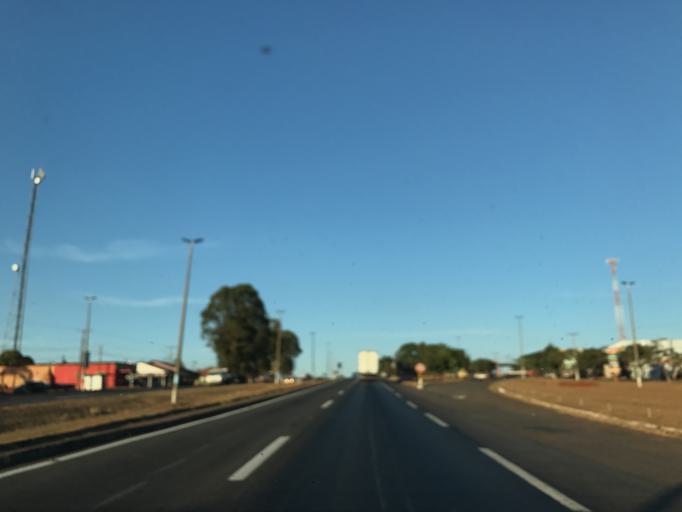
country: BR
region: Goias
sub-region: Goianapolis
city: Goianapolis
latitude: -16.4870
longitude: -49.0958
